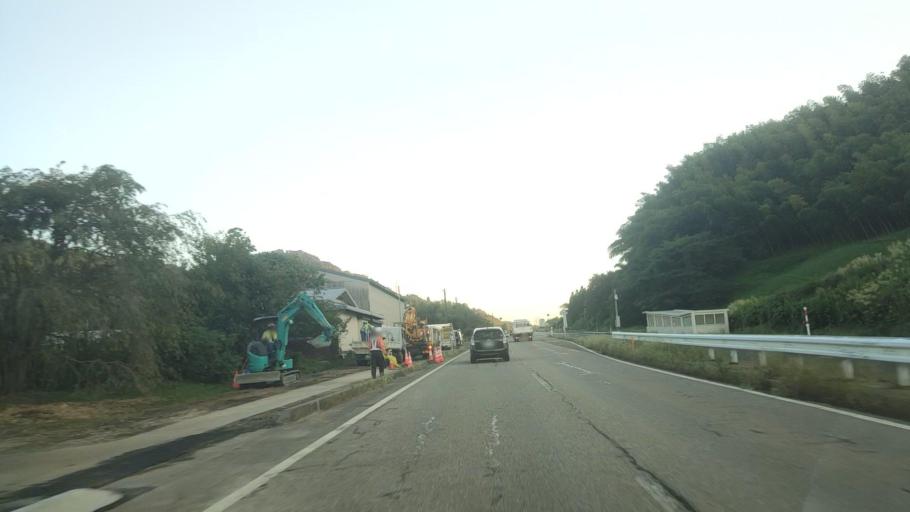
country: JP
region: Toyama
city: Takaoka
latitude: 36.8004
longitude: 137.0017
